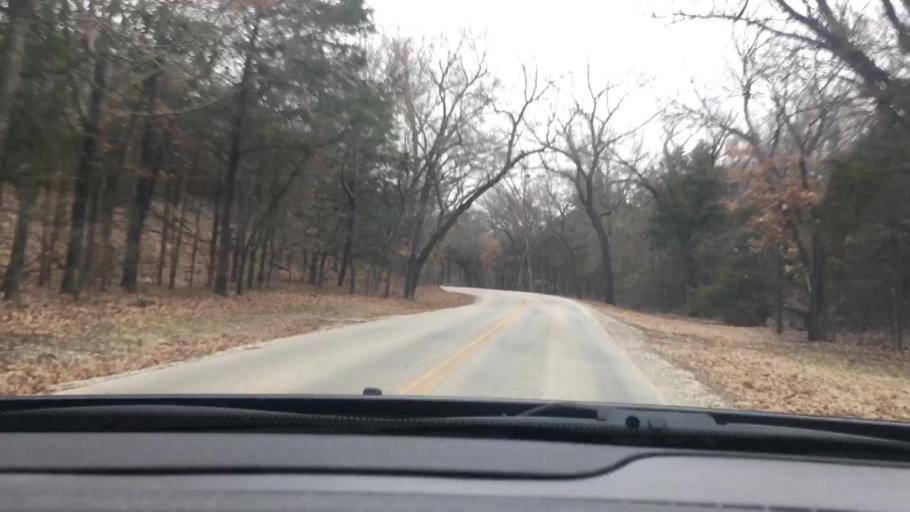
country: US
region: Oklahoma
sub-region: Murray County
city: Sulphur
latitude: 34.5037
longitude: -96.9665
